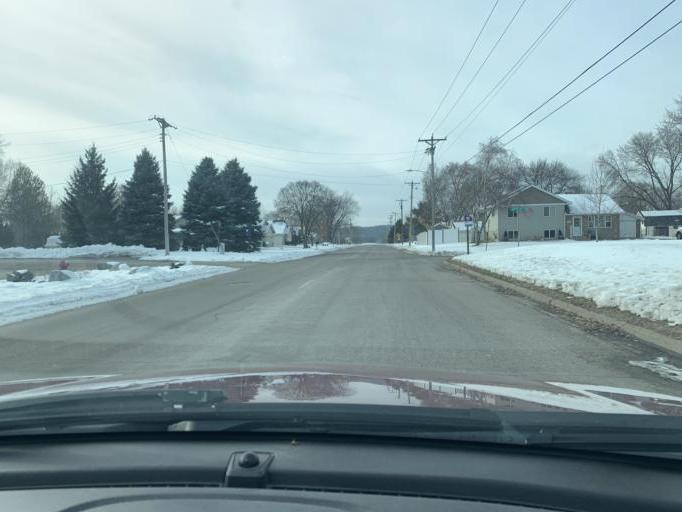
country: US
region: Minnesota
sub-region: Washington County
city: Saint Paul Park
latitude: 44.8262
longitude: -92.9813
